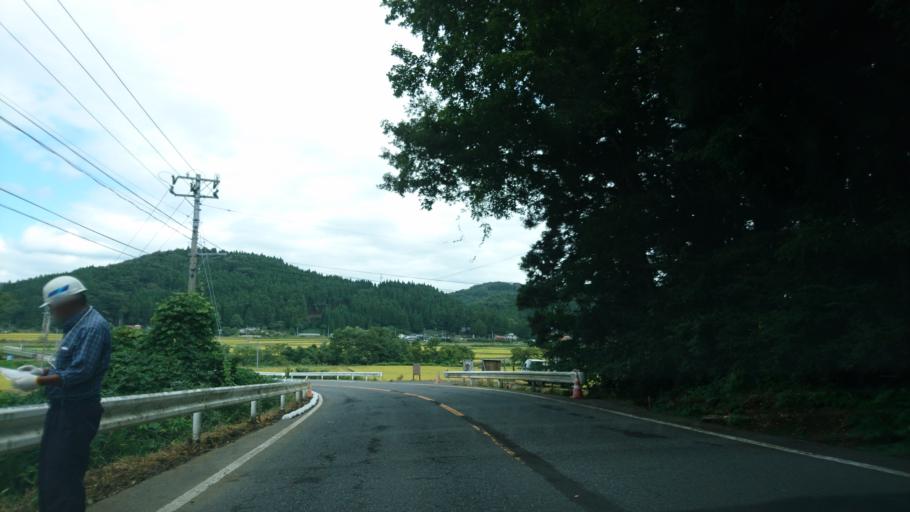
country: JP
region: Miyagi
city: Furukawa
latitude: 38.7619
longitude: 140.8645
